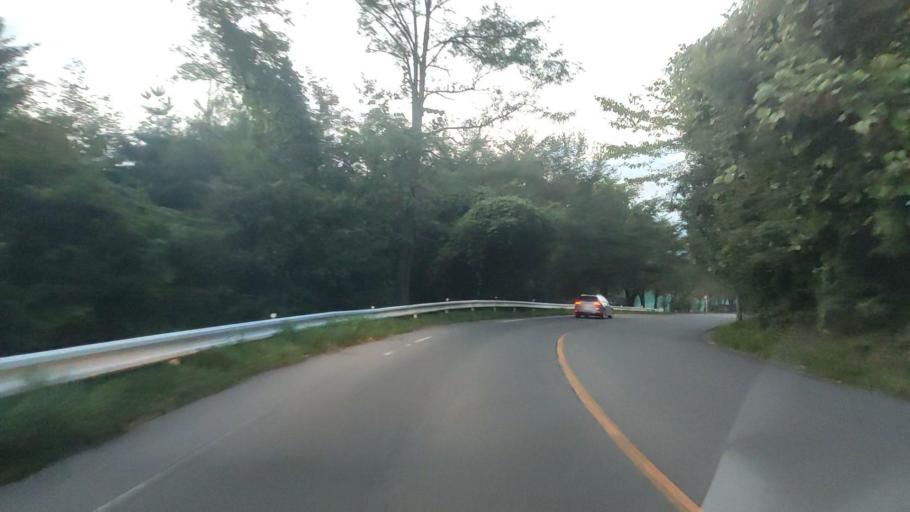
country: JP
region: Gunma
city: Nakanojomachi
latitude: 36.5349
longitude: 138.6087
